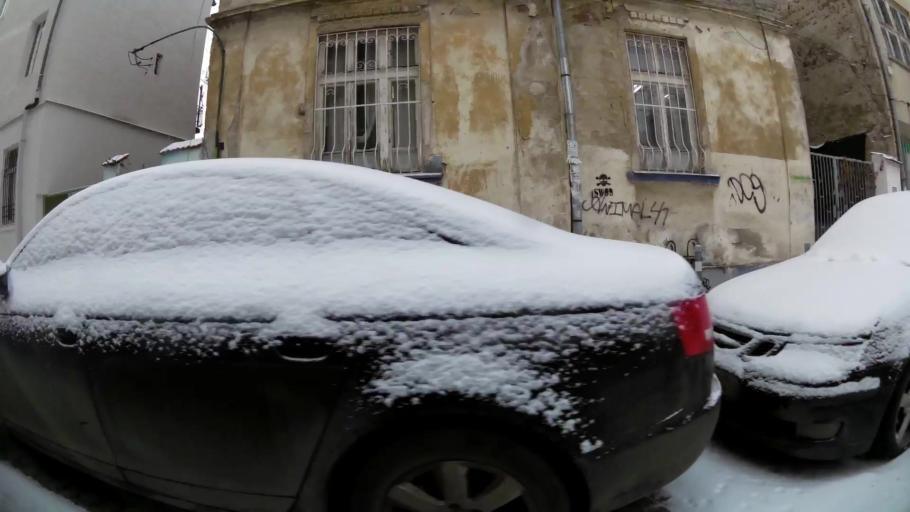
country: BG
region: Sofia-Capital
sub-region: Stolichna Obshtina
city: Sofia
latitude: 42.7024
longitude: 23.3280
